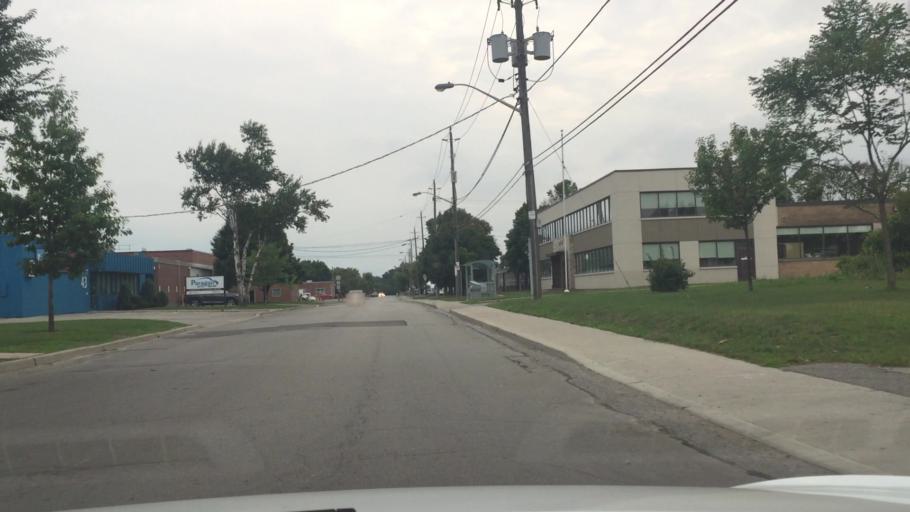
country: CA
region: Ontario
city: Scarborough
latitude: 43.7137
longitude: -79.3137
